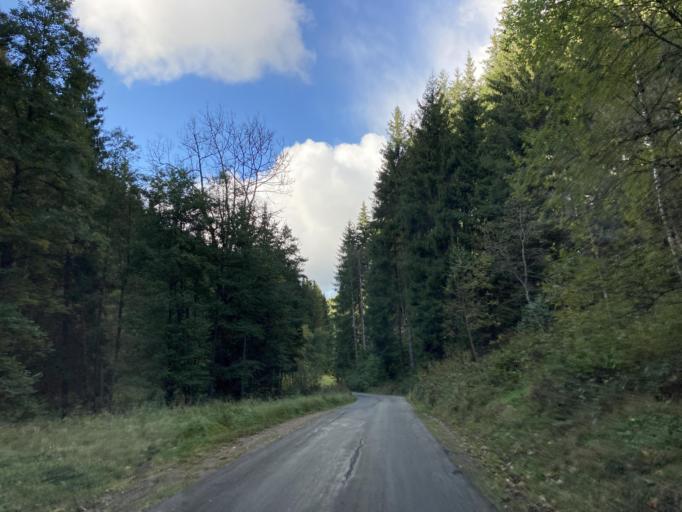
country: DE
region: Baden-Wuerttemberg
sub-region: Freiburg Region
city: Triberg im Schwarzwald
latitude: 48.1228
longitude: 8.2635
